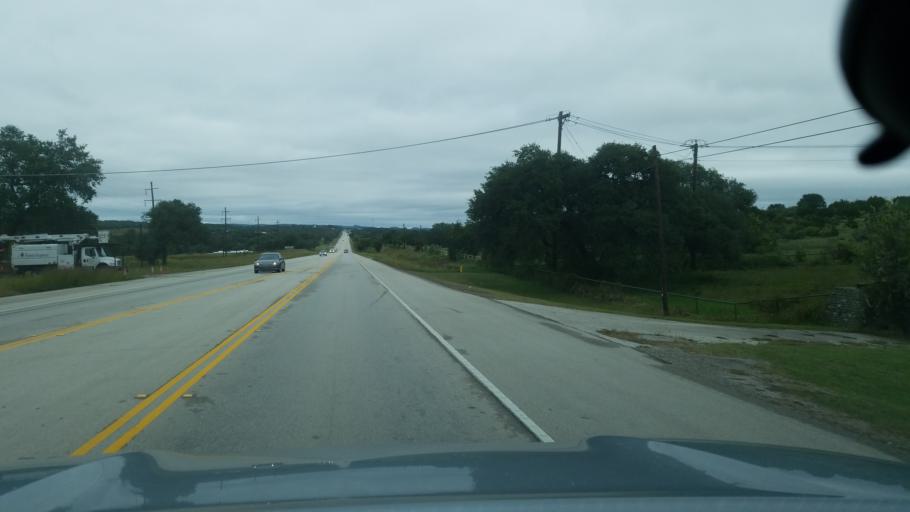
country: US
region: Texas
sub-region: Blanco County
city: Blanco
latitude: 30.0500
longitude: -98.4114
